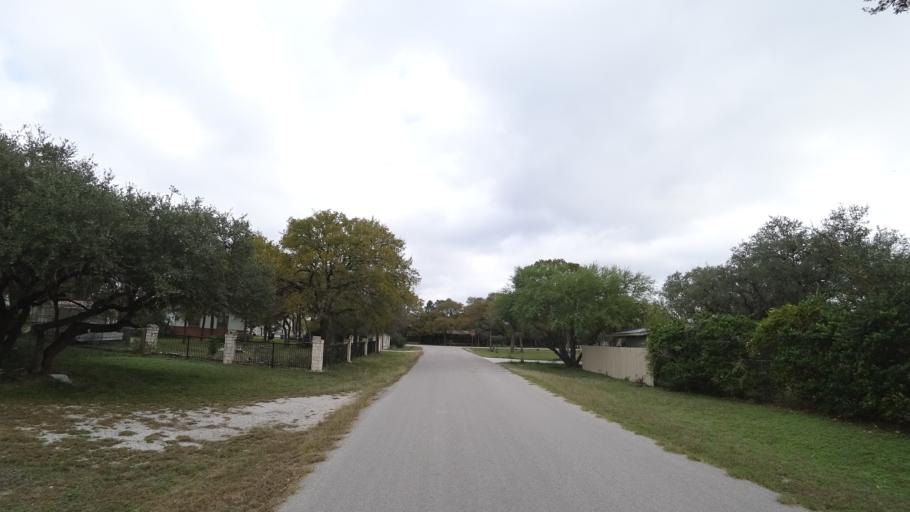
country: US
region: Texas
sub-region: Travis County
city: Bee Cave
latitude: 30.2525
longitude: -97.9220
